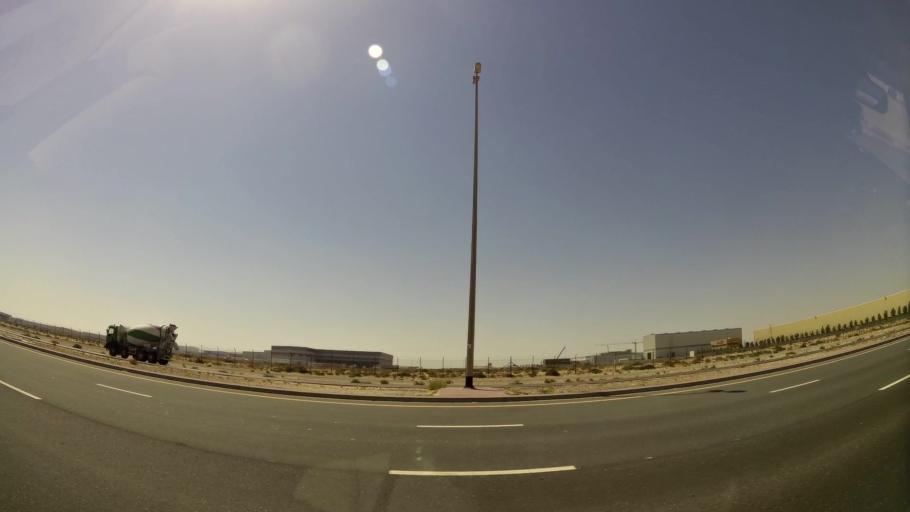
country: AE
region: Dubai
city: Dubai
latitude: 24.9384
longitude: 55.1018
